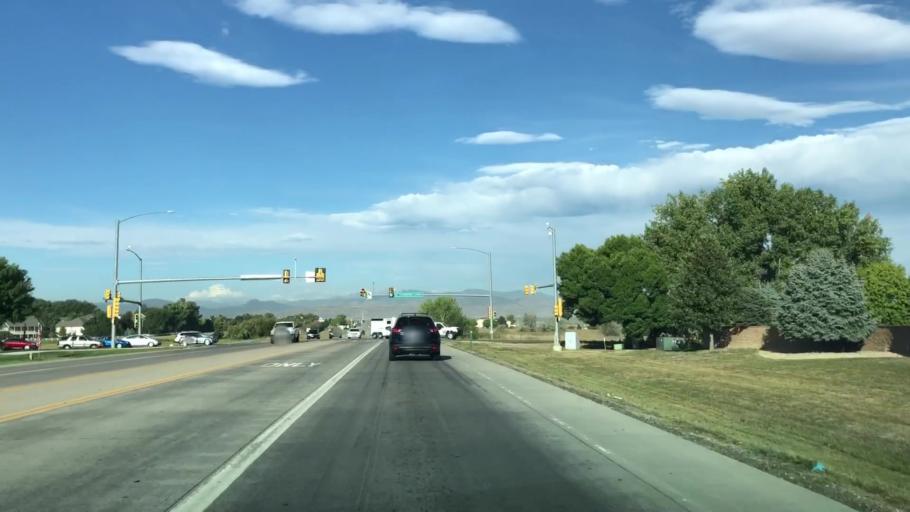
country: US
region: Colorado
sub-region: Weld County
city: Windsor
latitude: 40.4795
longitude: -104.9810
